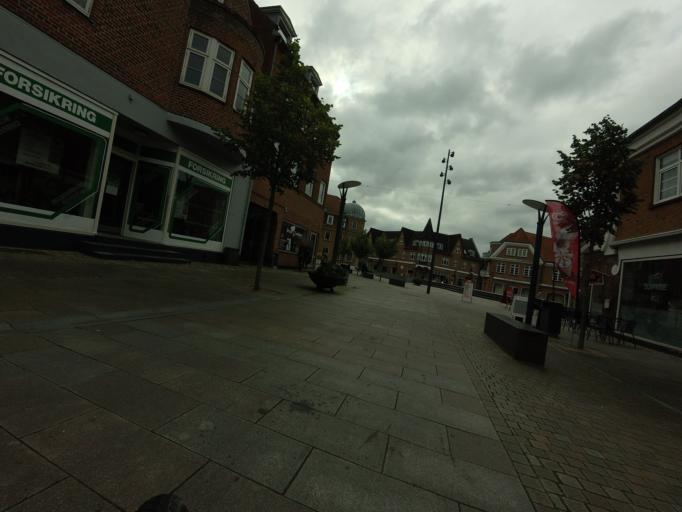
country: DK
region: South Denmark
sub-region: Billund Kommune
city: Grindsted
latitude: 55.7577
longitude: 8.9288
